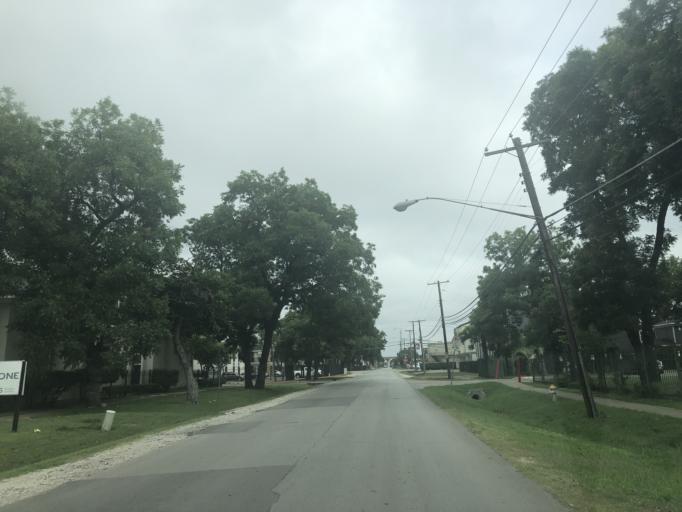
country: US
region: Texas
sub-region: Dallas County
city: University Park
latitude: 32.8561
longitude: -96.8737
